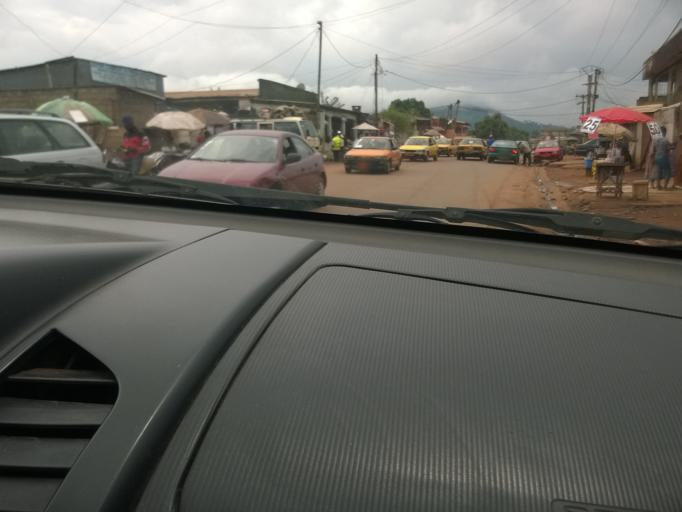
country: CM
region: Centre
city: Yaounde
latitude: 3.9065
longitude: 11.5305
